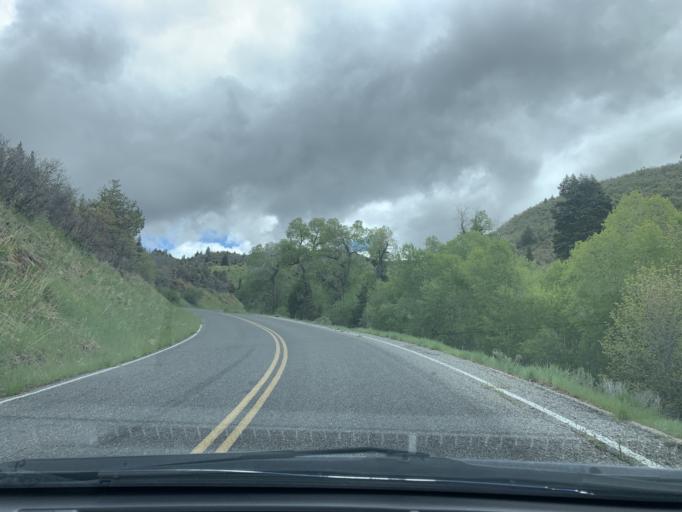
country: US
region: Utah
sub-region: Juab County
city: Nephi
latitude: 39.7790
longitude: -111.6946
